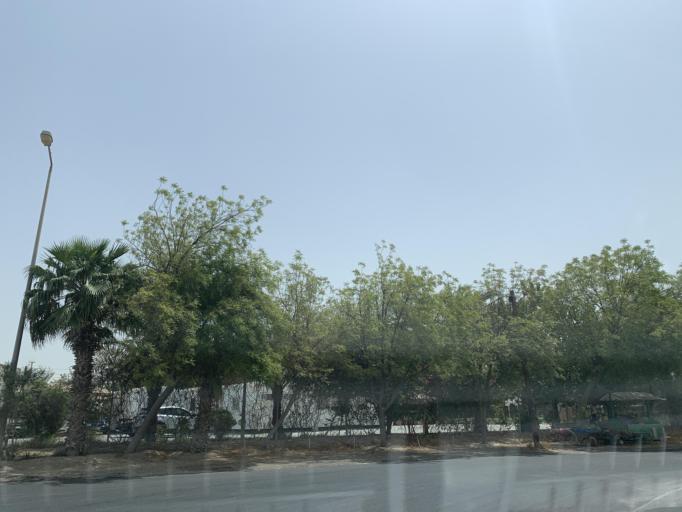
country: BH
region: Northern
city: Madinat `Isa
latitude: 26.1642
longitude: 50.5276
